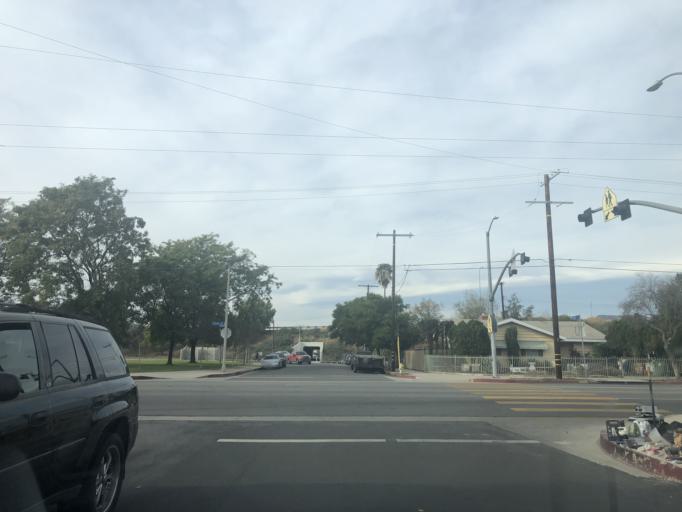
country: US
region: California
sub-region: Los Angeles County
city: San Fernando
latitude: 34.2670
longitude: -118.4350
